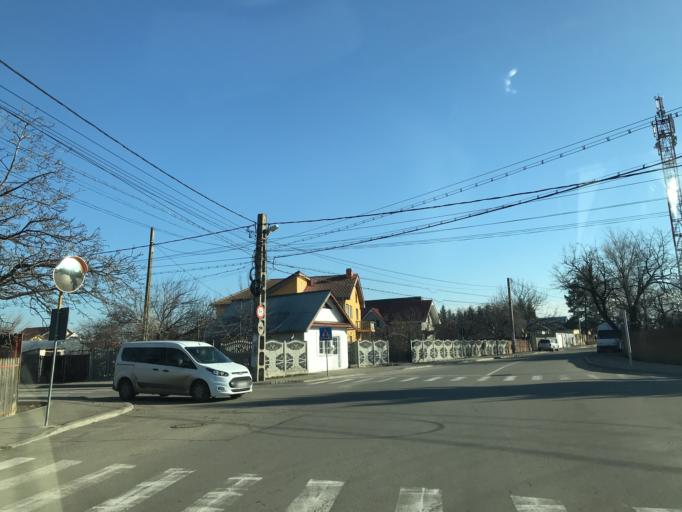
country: RO
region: Olt
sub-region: Municipiul Slatina
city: Slatina
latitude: 44.4172
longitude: 24.3717
